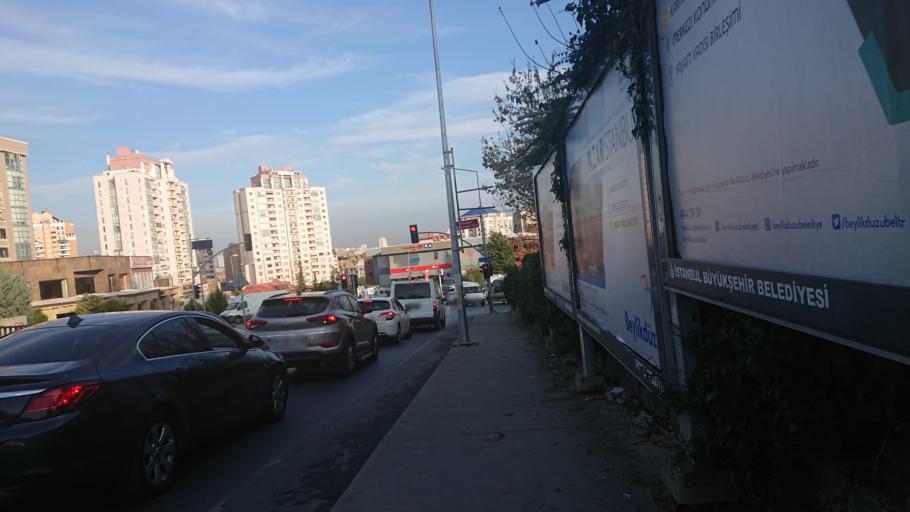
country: TR
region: Istanbul
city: Esenyurt
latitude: 41.0625
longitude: 28.6818
